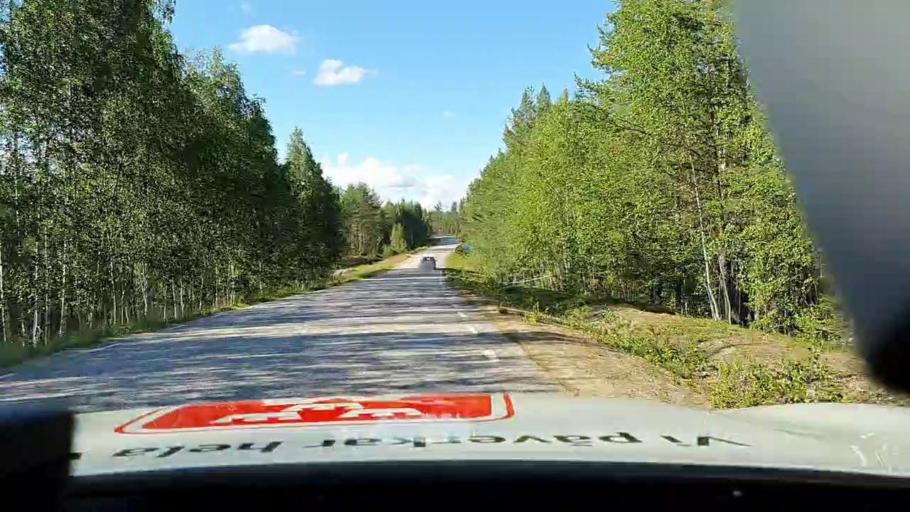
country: SE
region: Norrbotten
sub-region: Overkalix Kommun
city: OEverkalix
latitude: 66.2427
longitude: 22.9247
